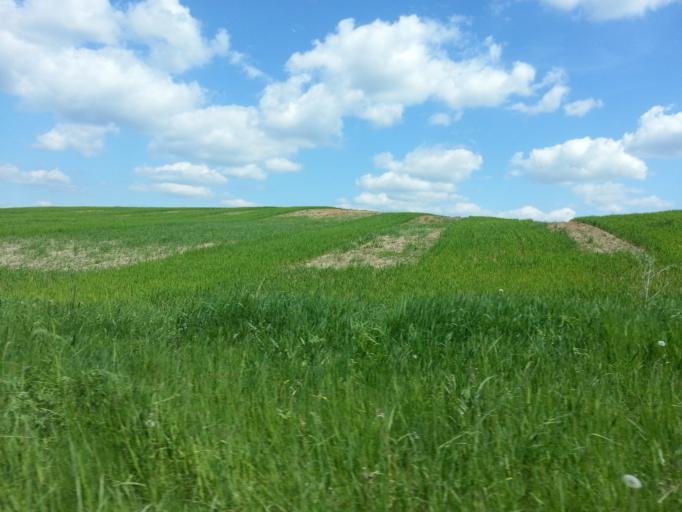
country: LT
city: Trakai
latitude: 54.6802
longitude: 24.9852
